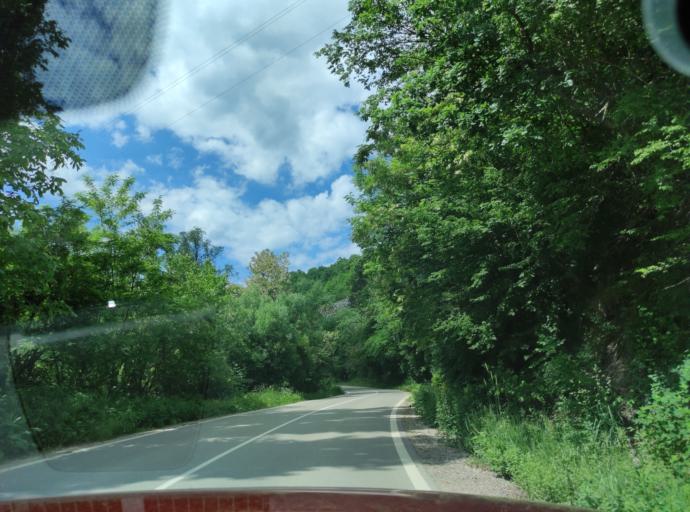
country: BG
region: Montana
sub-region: Obshtina Chiprovtsi
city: Chiprovtsi
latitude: 43.4408
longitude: 22.9351
